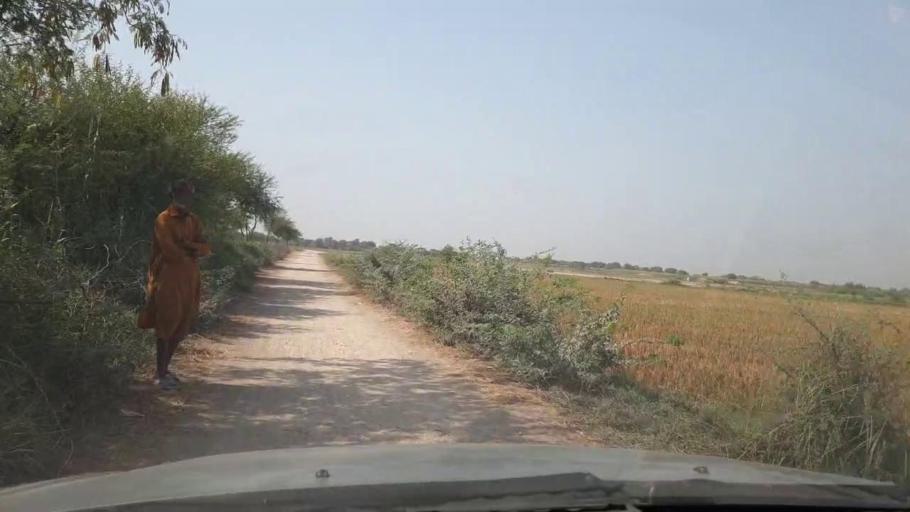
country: PK
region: Sindh
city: Bulri
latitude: 24.8740
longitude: 68.3146
